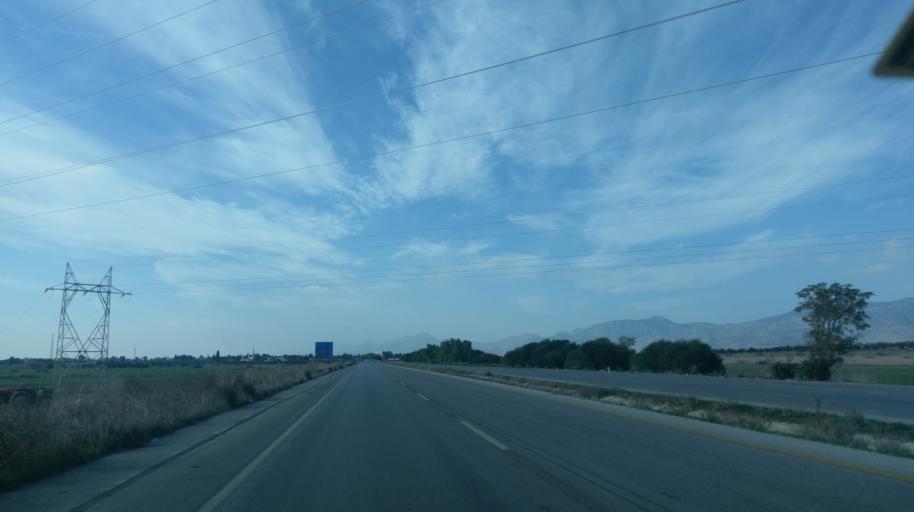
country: CY
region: Ammochostos
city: Lefkonoiko
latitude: 35.2011
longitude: 33.6047
